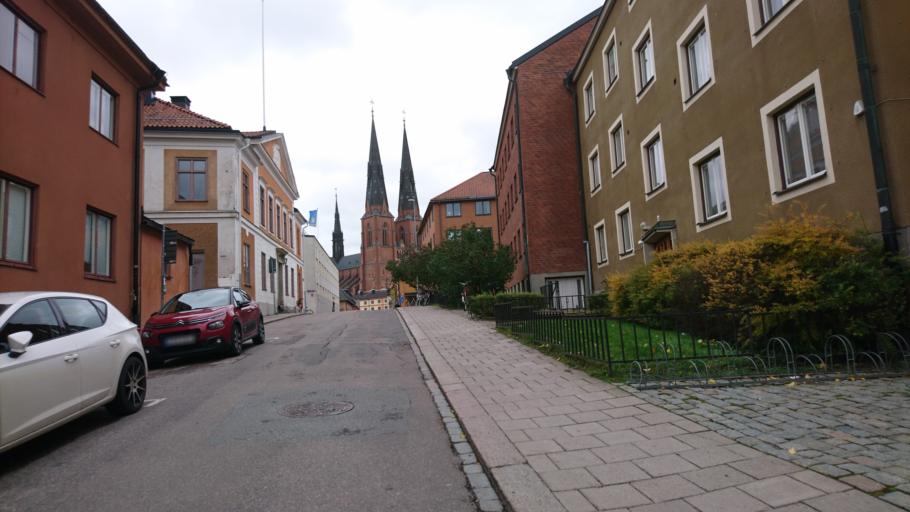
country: SE
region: Uppsala
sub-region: Uppsala Kommun
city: Uppsala
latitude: 59.8599
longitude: 17.6287
